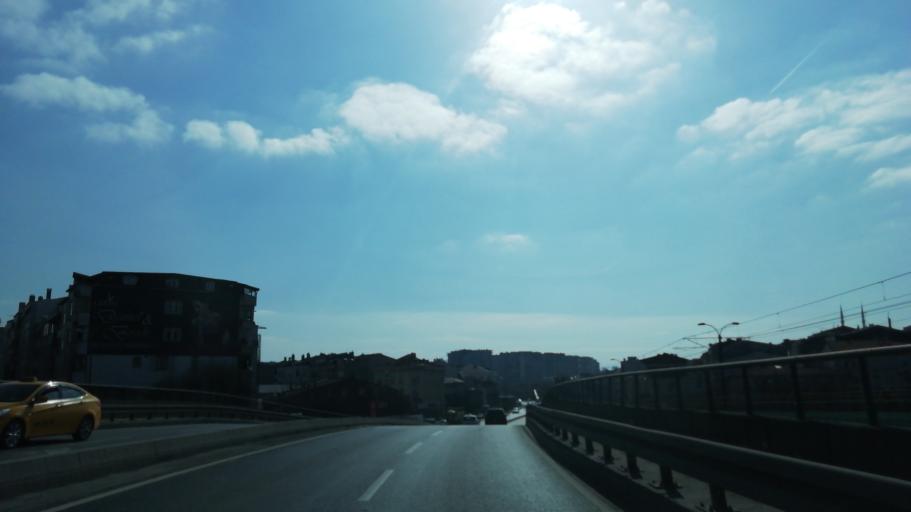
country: TR
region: Istanbul
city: Esenler
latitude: 41.0340
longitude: 28.8962
